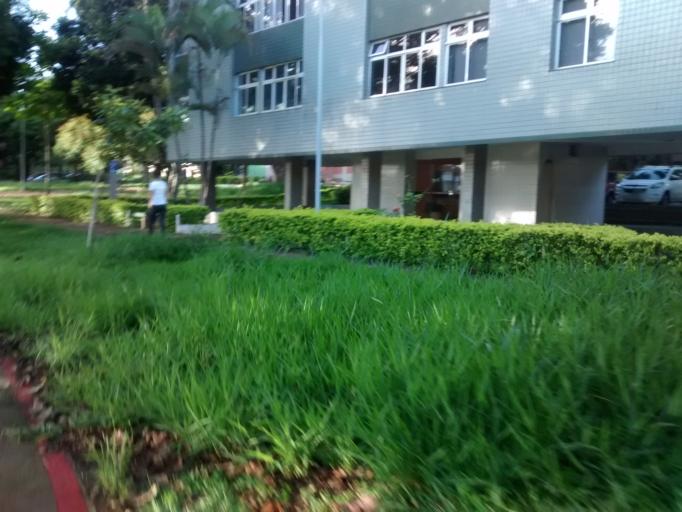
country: BR
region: Federal District
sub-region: Brasilia
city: Brasilia
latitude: -15.7544
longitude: -47.8800
